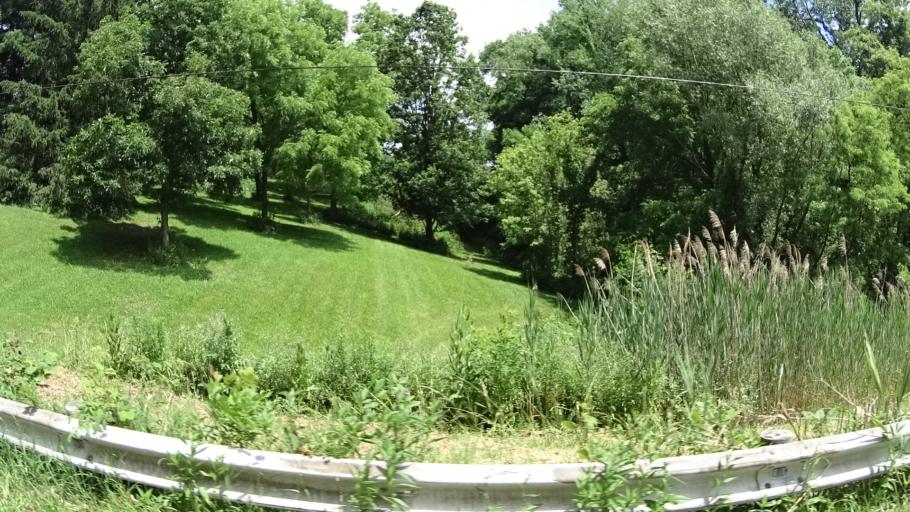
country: US
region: Ohio
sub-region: Erie County
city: Milan
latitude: 41.3159
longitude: -82.5817
